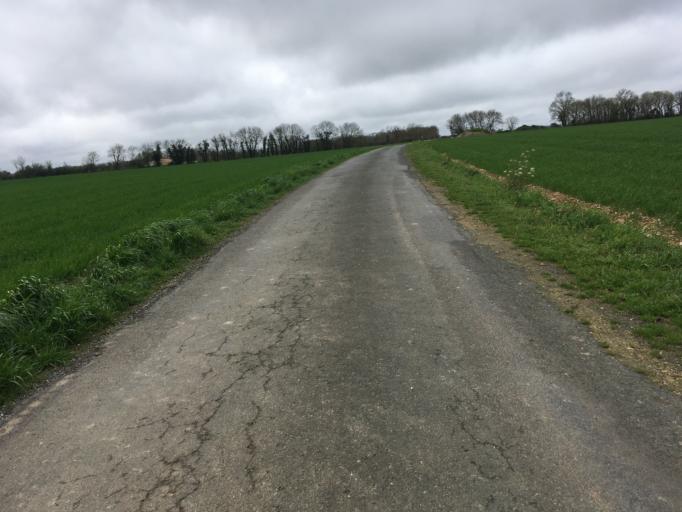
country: FR
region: Poitou-Charentes
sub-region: Departement de la Charente-Maritime
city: Saint-Germain-de-Marencennes
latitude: 46.1166
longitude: -0.8262
